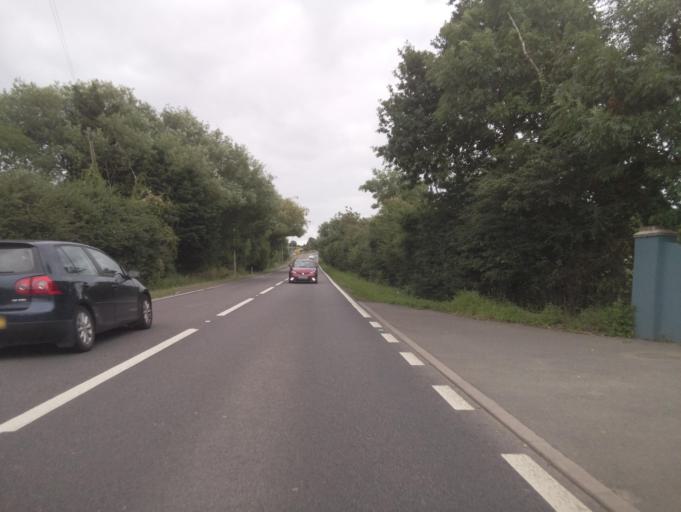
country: GB
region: England
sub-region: Lincolnshire
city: Barrowby
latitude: 52.9242
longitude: -0.6949
